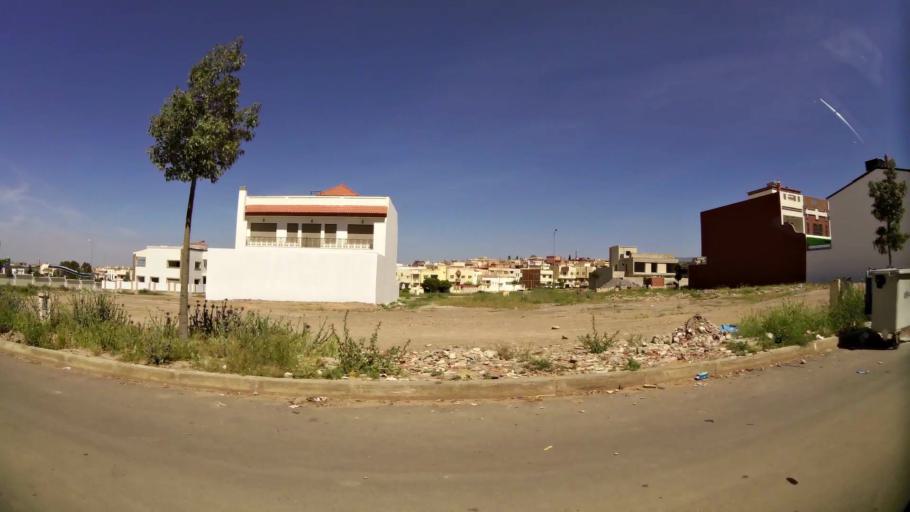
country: MA
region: Oriental
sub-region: Oujda-Angad
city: Oujda
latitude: 34.6539
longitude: -1.9095
